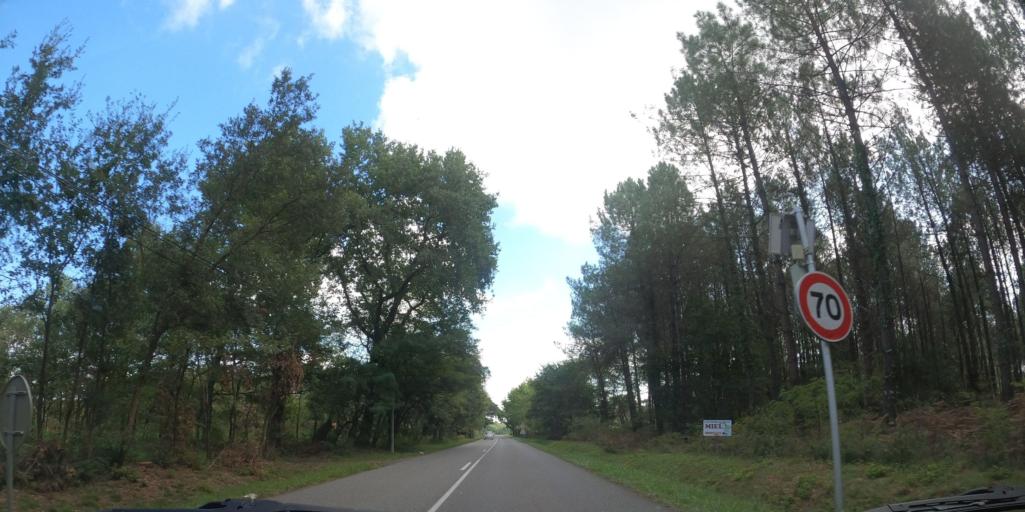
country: FR
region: Aquitaine
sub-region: Departement des Landes
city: Soustons
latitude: 43.7343
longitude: -1.2904
